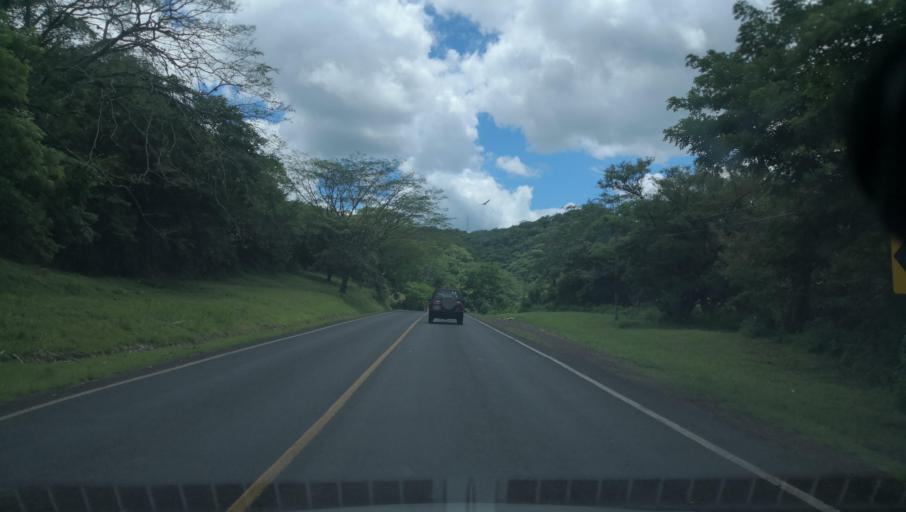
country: NI
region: Esteli
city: Condega
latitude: 13.3071
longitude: -86.3496
